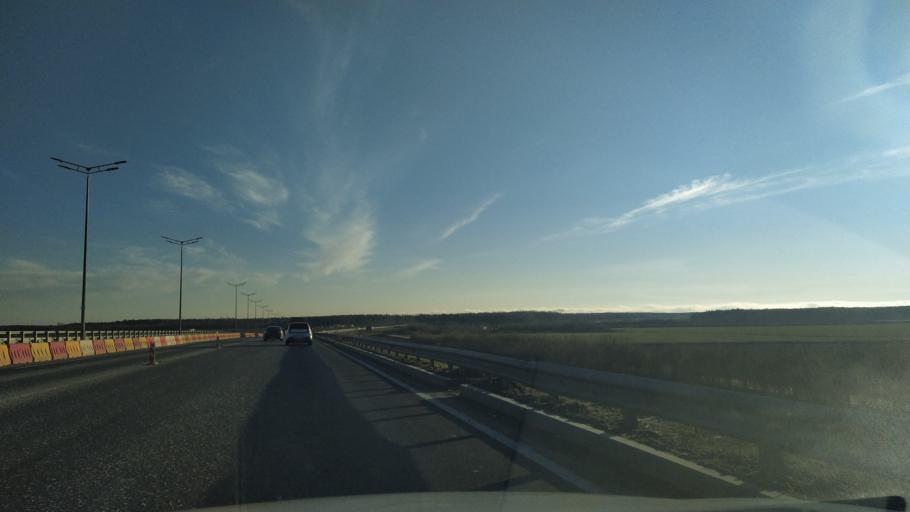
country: RU
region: St.-Petersburg
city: Pargolovo
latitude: 60.0913
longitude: 30.2433
